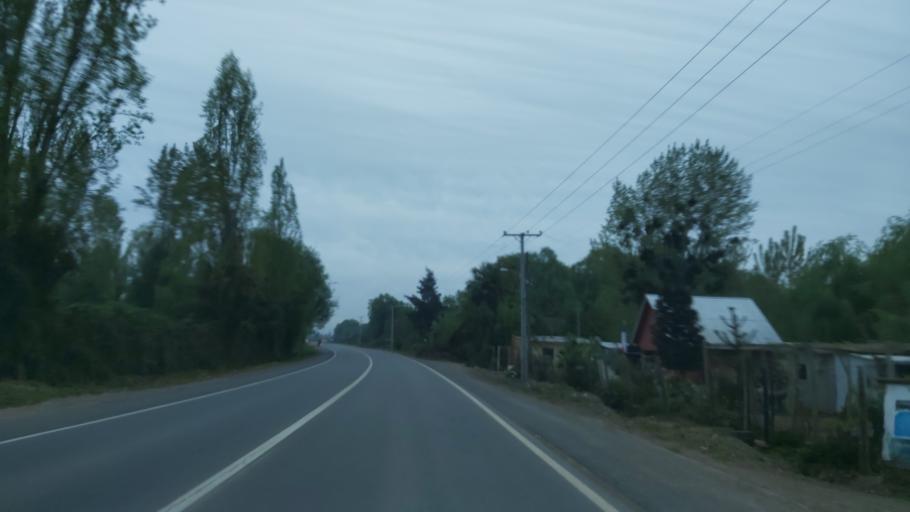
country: CL
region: Maule
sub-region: Provincia de Linares
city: Linares
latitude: -35.7610
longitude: -71.5076
